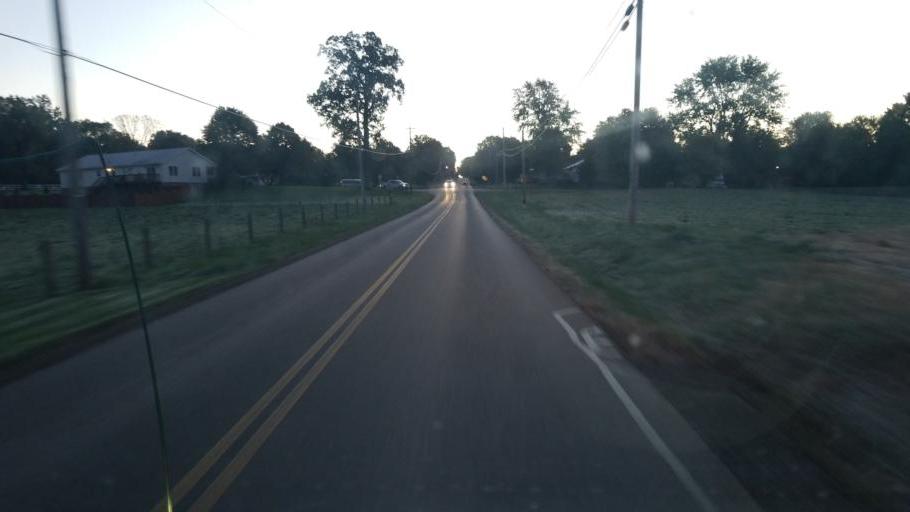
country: US
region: Ohio
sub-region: Wayne County
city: Apple Creek
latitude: 40.7409
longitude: -81.8176
